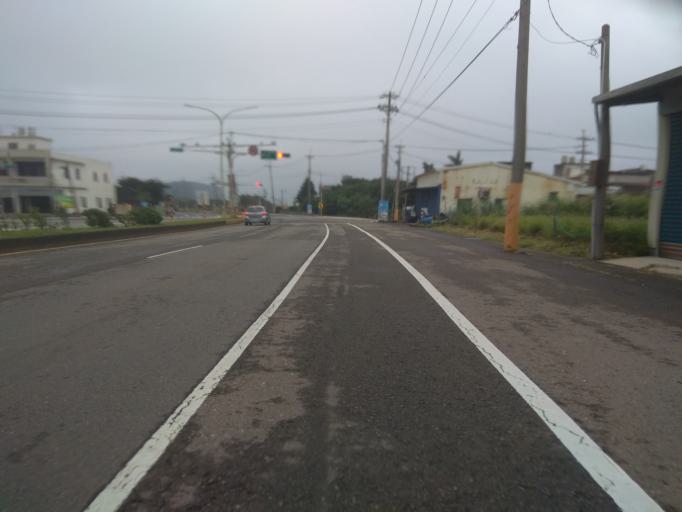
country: TW
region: Taiwan
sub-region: Hsinchu
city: Zhubei
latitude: 25.0313
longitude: 121.0758
